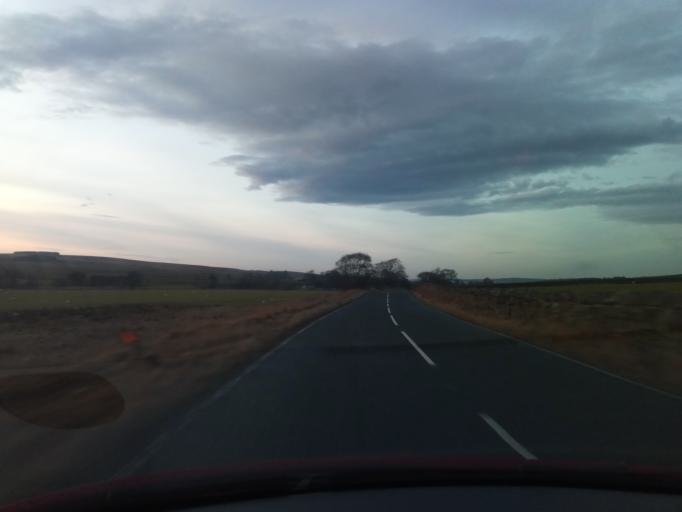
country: GB
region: England
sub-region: Northumberland
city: Otterburn
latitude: 55.2408
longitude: -2.2105
